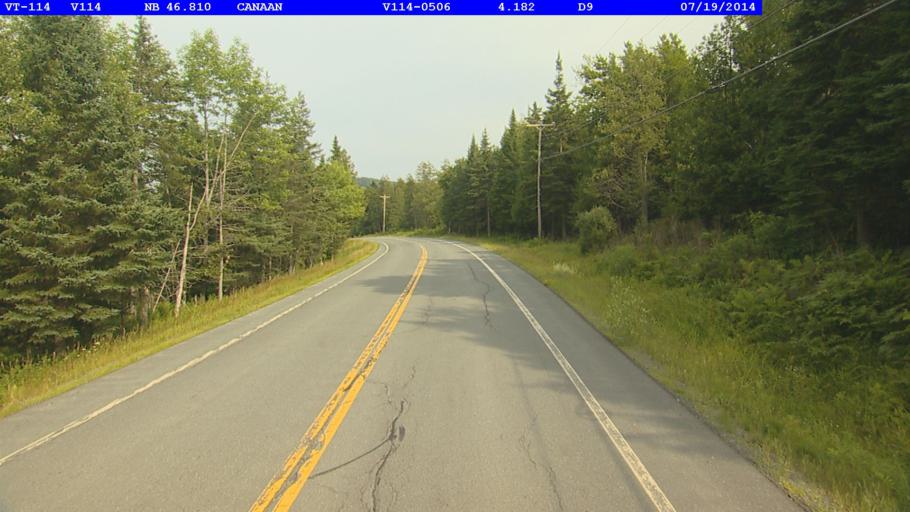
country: US
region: New Hampshire
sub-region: Coos County
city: Colebrook
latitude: 45.0082
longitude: -71.6107
